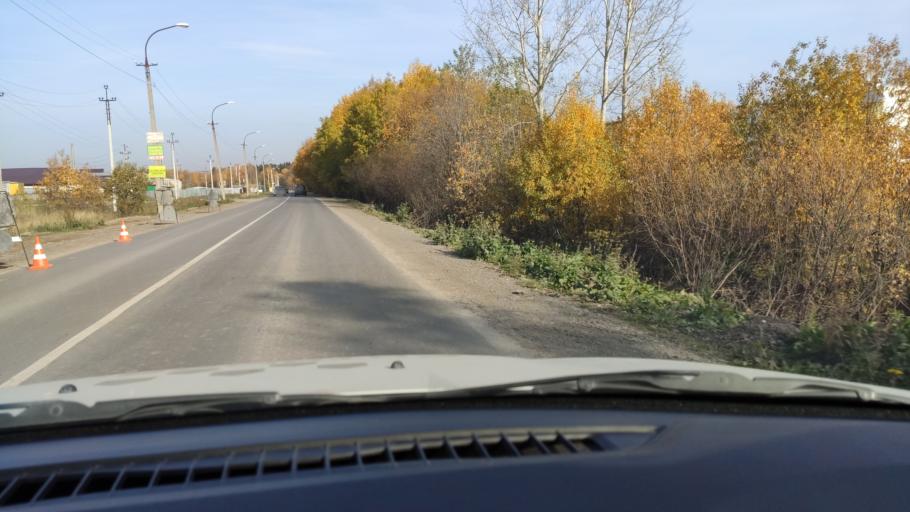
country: RU
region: Perm
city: Sylva
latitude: 58.0266
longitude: 56.7389
